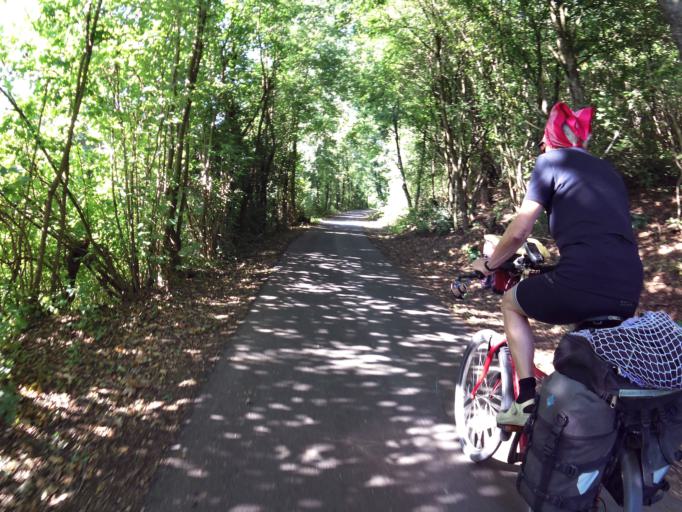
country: DE
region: Baden-Wuerttemberg
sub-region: Tuebingen Region
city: Rottenburg
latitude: 48.4616
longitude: 8.8977
